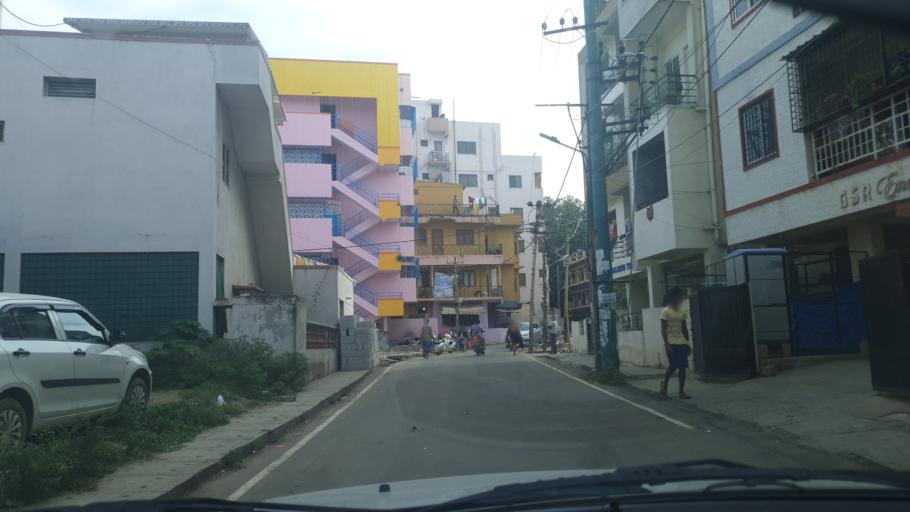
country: IN
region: Karnataka
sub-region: Bangalore Urban
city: Bangalore
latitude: 12.9656
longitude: 77.6727
